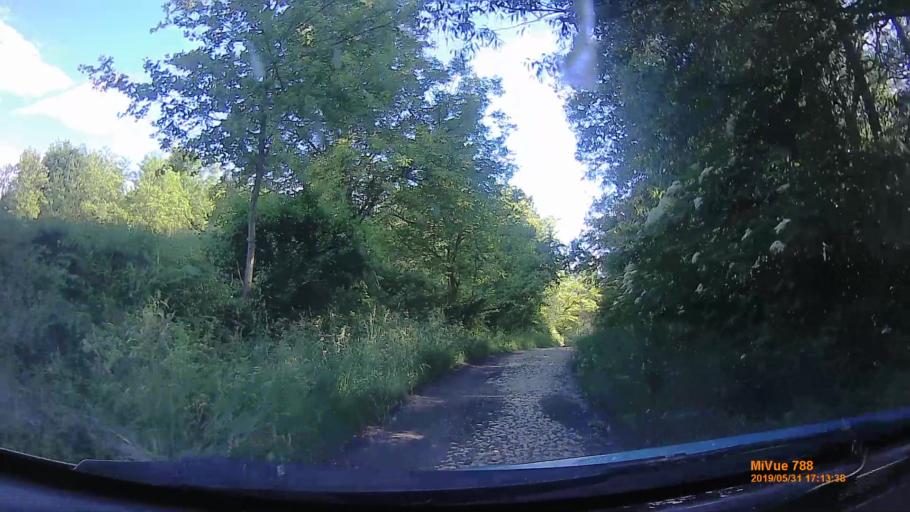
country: HU
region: Nograd
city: Nagyoroszi
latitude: 48.0353
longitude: 19.0471
